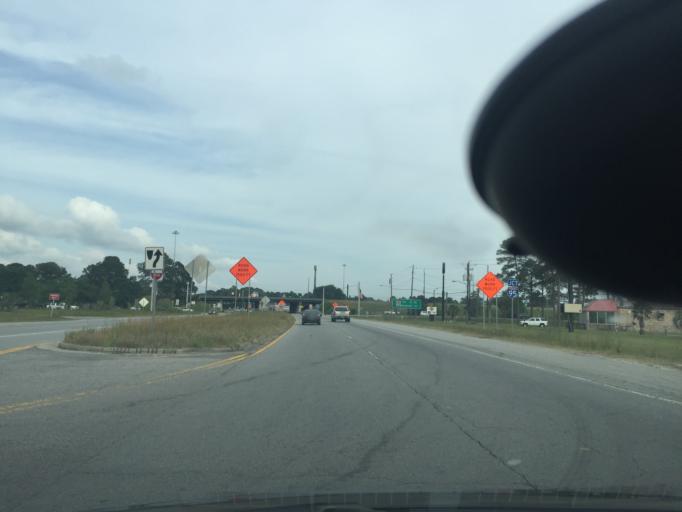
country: US
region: Georgia
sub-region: Chatham County
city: Georgetown
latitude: 32.0057
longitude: -81.2862
